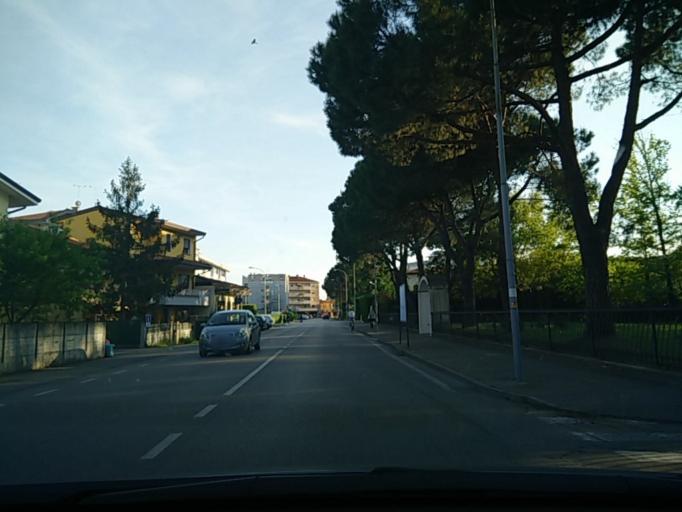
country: IT
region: Veneto
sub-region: Provincia di Venezia
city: San Dona di Piave
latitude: 45.6328
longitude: 12.5768
